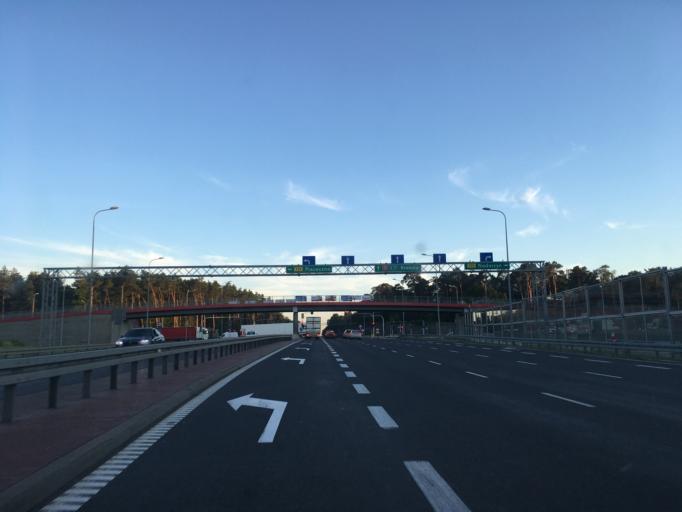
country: PL
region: Masovian Voivodeship
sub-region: Powiat piaseczynski
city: Lesznowola
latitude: 52.1028
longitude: 20.8864
